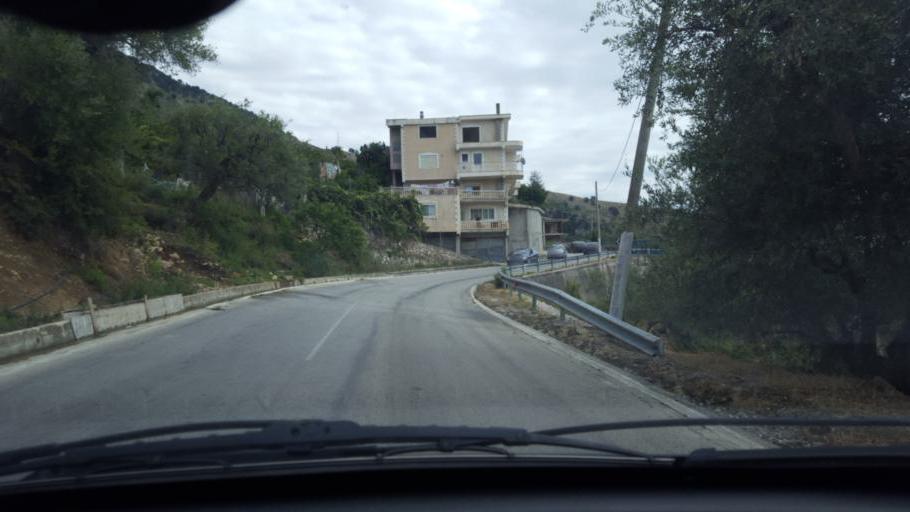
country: AL
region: Vlore
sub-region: Rrethi i Sarandes
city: Lukove
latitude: 40.0552
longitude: 19.8663
